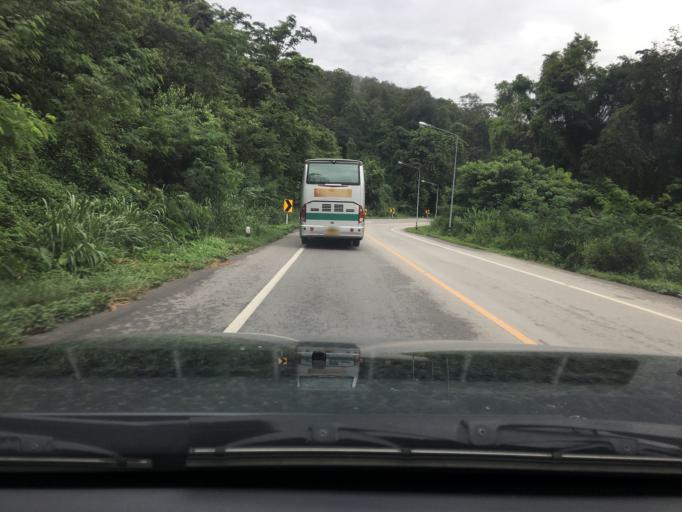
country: TH
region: Chiang Mai
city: Mae On
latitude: 19.0034
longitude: 99.2887
